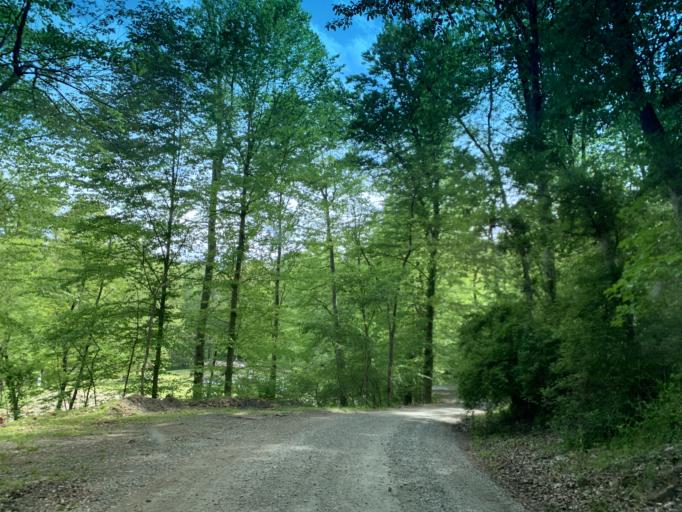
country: US
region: Maryland
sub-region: Harford County
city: South Bel Air
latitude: 39.6174
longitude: -76.2888
